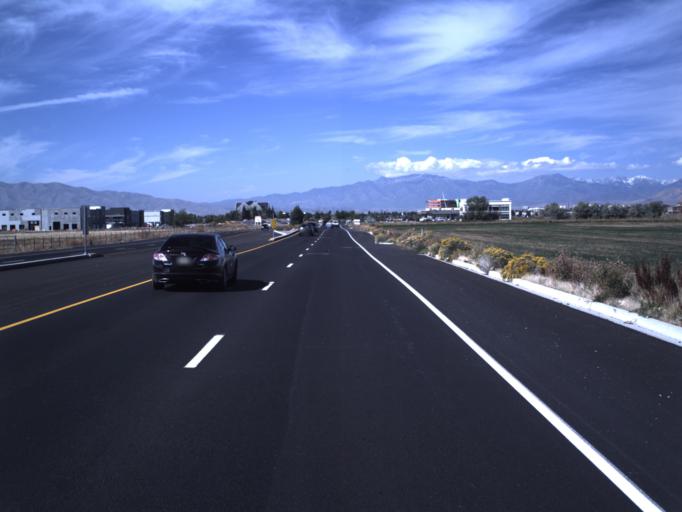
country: US
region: Utah
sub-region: Utah County
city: Pleasant Grove
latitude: 40.3508
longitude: -111.7510
